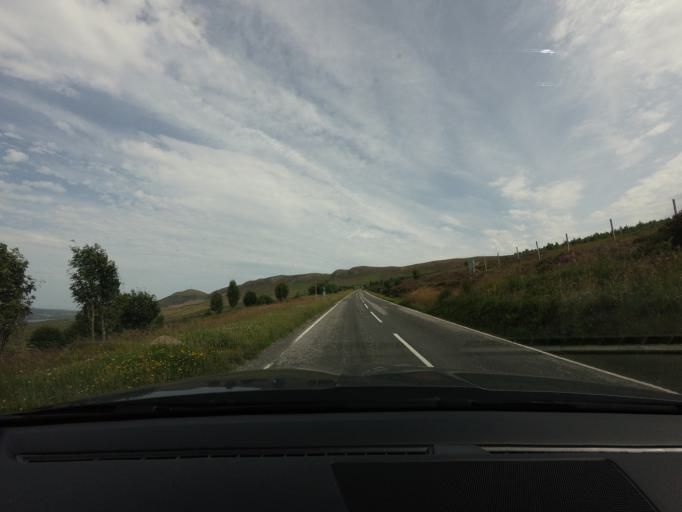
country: GB
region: Scotland
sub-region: Highland
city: Alness
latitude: 57.8426
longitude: -4.2795
